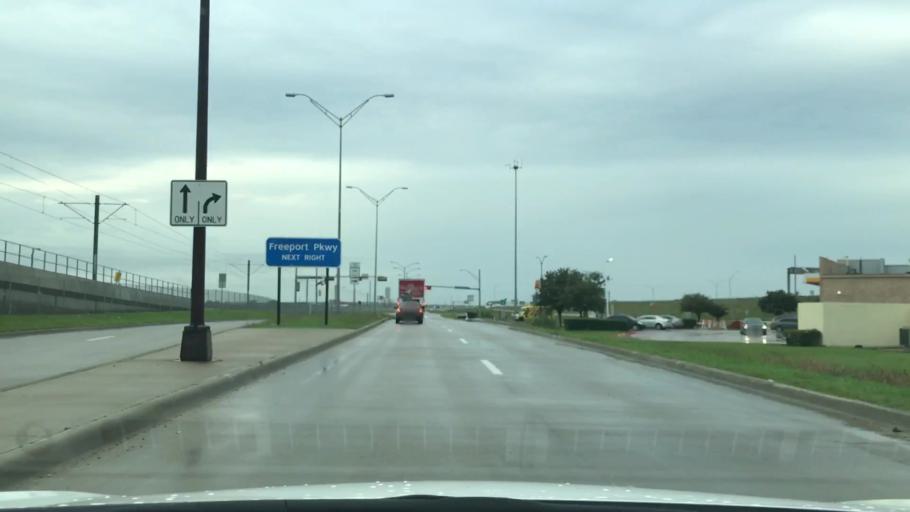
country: US
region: Texas
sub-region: Dallas County
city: Coppell
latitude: 32.9192
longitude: -97.0202
